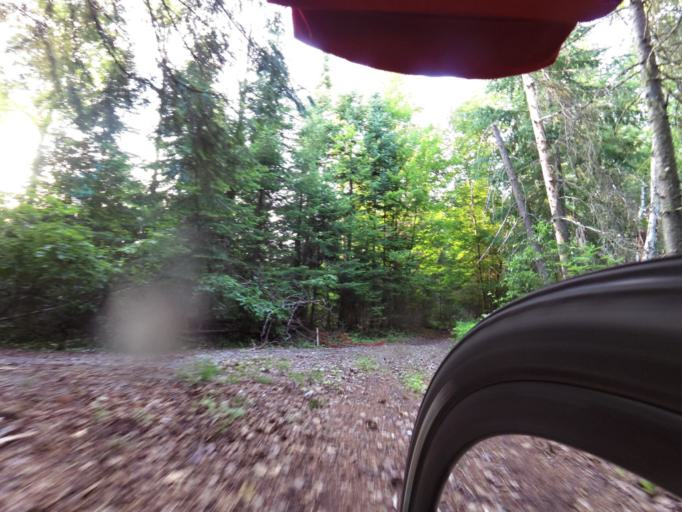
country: CA
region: Quebec
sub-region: Laurentides
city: Riviere-Rouge
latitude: 46.3947
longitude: -75.0231
